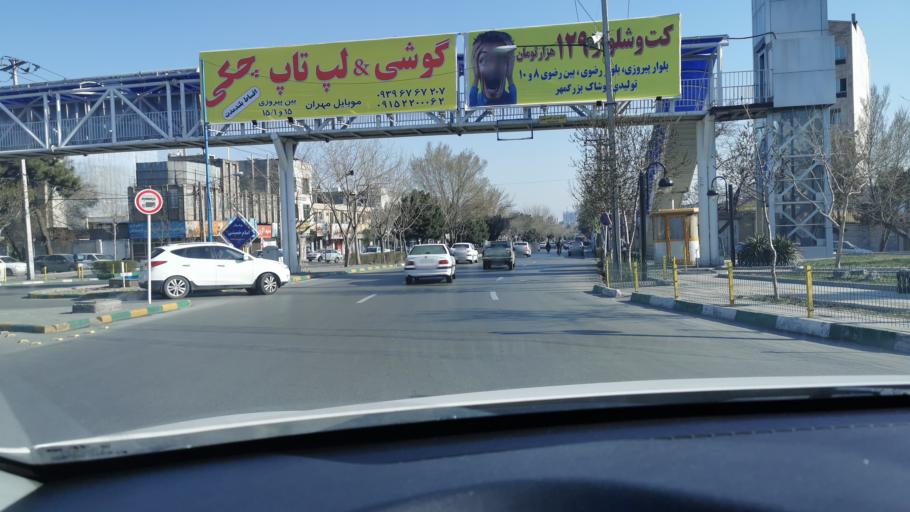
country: IR
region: Razavi Khorasan
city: Mashhad
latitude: 36.2642
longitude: 59.5855
